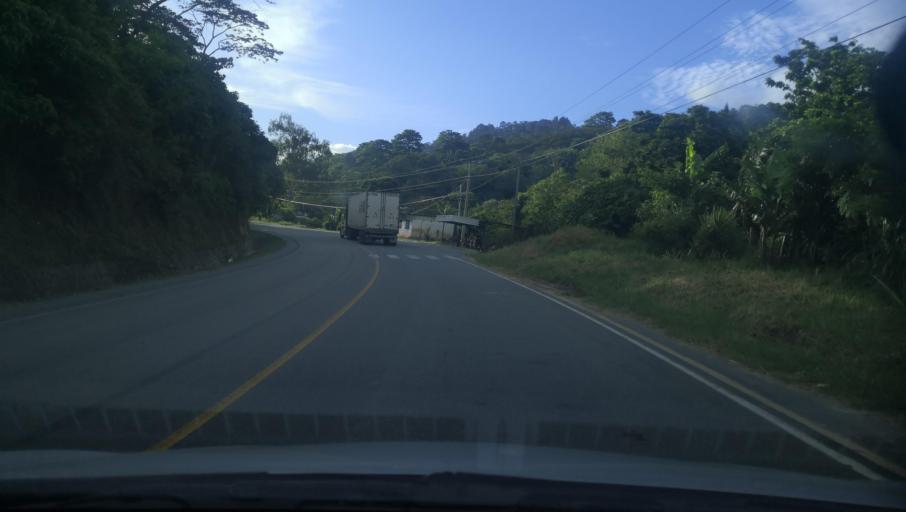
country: HN
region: El Paraiso
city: El Paraiso
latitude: 13.7851
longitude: -86.5602
